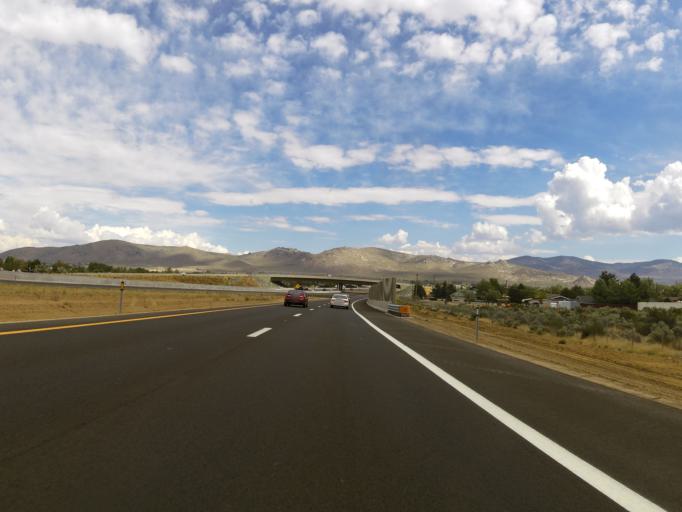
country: US
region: Nevada
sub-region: Douglas County
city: Indian Hills
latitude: 39.1209
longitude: -119.7662
